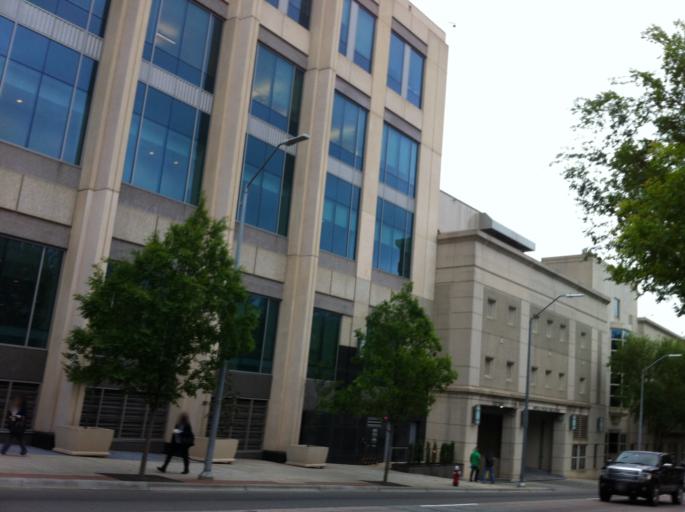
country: US
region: North Carolina
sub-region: Wake County
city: Raleigh
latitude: 35.7767
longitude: -78.6420
